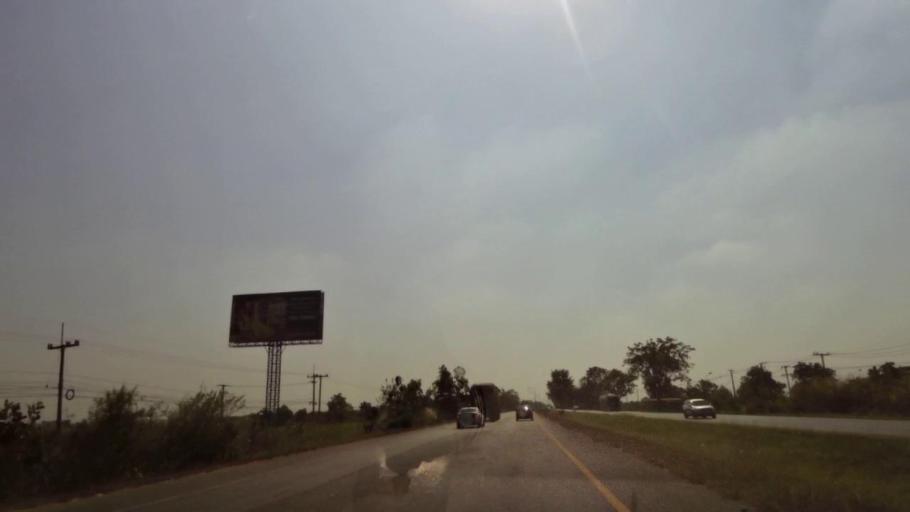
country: TH
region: Phichit
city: Wachira Barami
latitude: 16.4653
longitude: 100.1473
